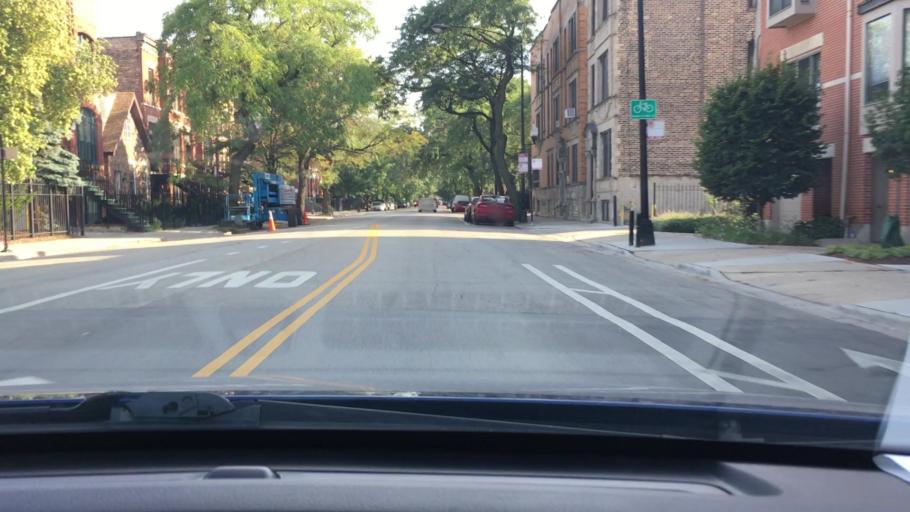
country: US
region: Illinois
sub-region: Cook County
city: Chicago
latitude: 41.8740
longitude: -87.6618
